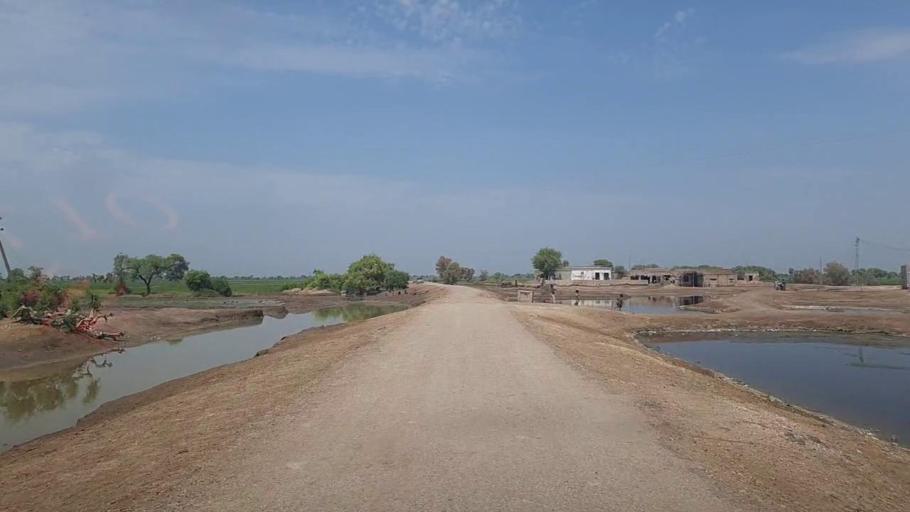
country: PK
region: Sindh
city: Thul
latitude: 28.2940
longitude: 68.6819
